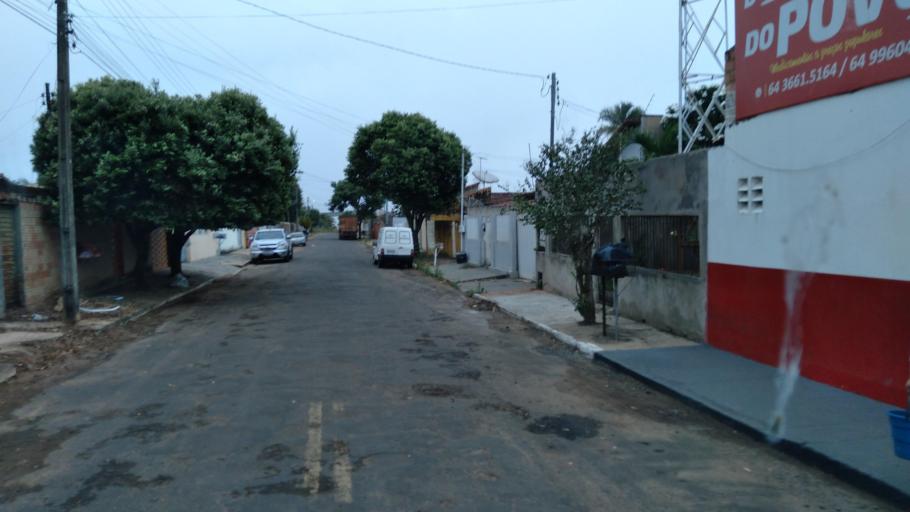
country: BR
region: Goias
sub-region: Mineiros
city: Mineiros
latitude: -17.5735
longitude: -52.5393
